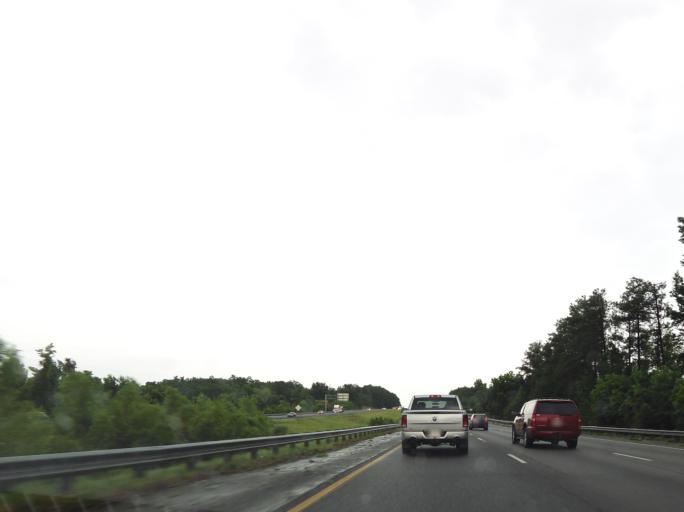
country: US
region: Georgia
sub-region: Houston County
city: Perry
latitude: 32.5312
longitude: -83.7438
